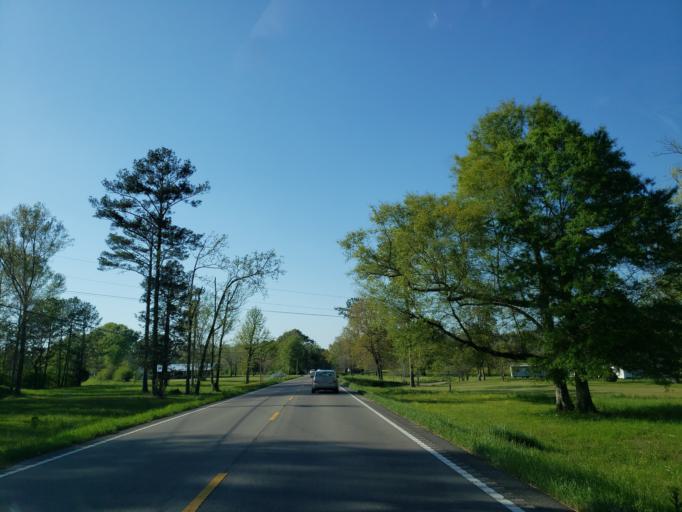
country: US
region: Mississippi
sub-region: Jones County
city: Laurel
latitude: 31.6239
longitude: -89.0882
